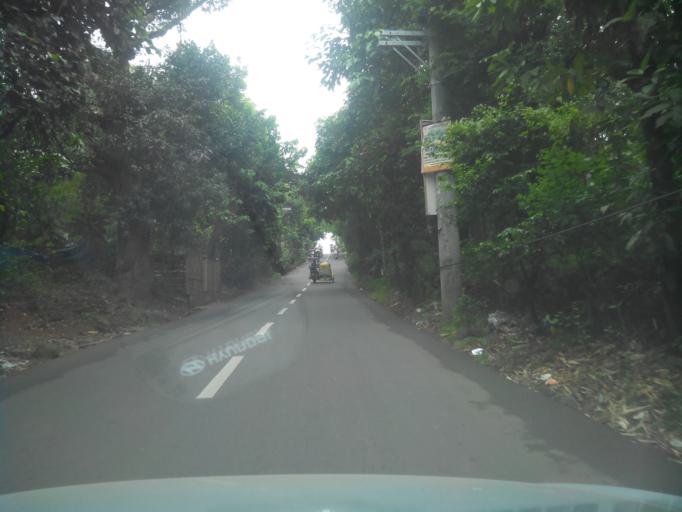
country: PH
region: Calabarzon
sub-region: Province of Rizal
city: Teresa
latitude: 14.5994
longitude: 121.1820
